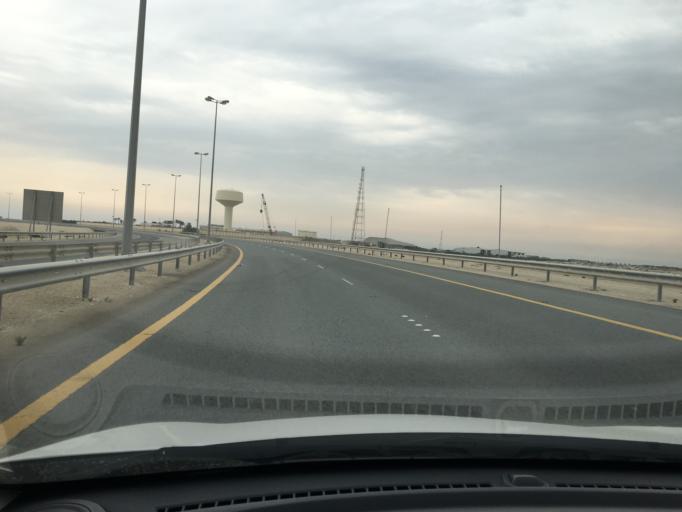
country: BH
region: Central Governorate
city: Dar Kulayb
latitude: 25.8430
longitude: 50.5843
